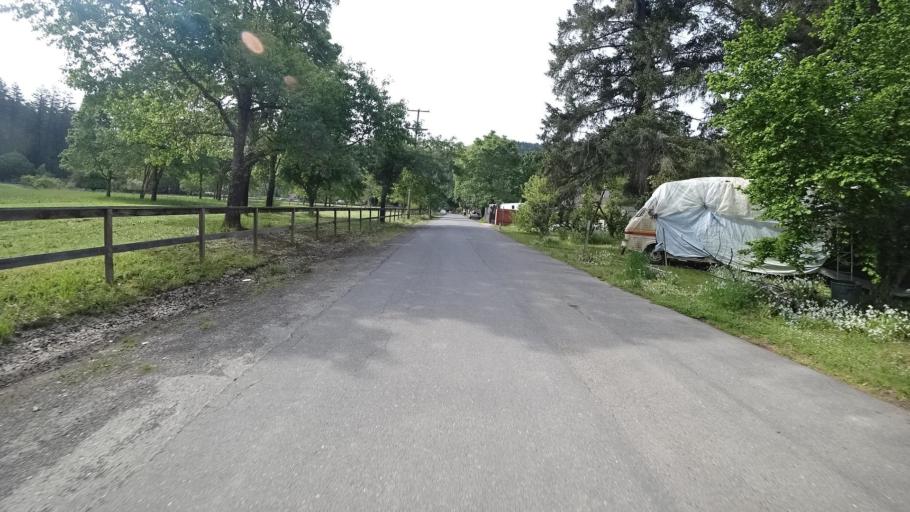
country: US
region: California
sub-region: Humboldt County
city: Redway
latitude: 40.2101
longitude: -123.7898
